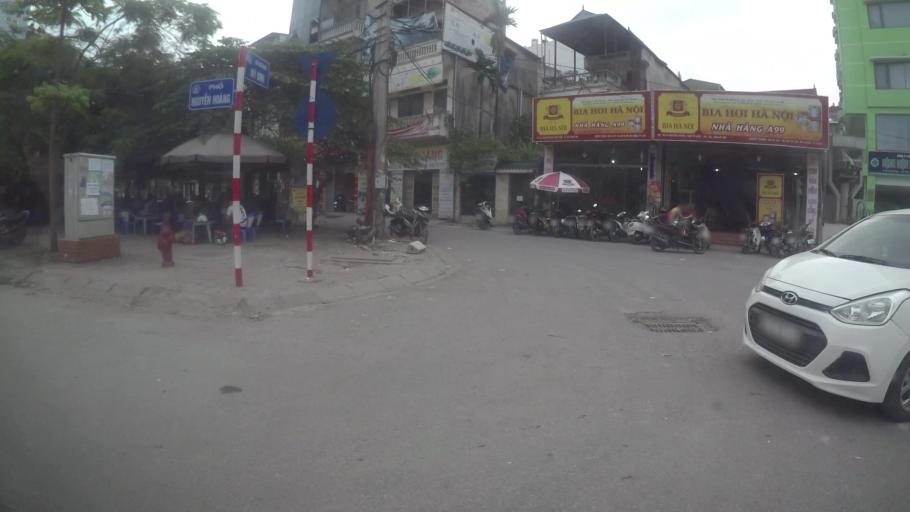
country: VN
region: Ha Noi
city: Cau Dien
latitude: 21.0314
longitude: 105.7742
